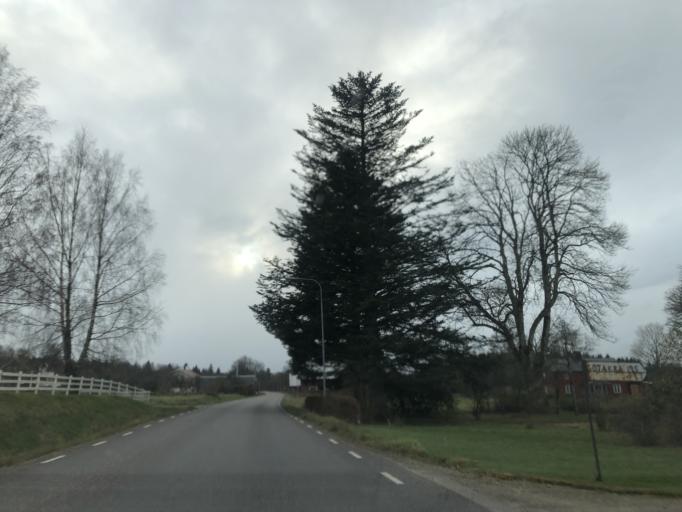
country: SE
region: Vaestra Goetaland
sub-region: Ulricehamns Kommun
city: Ulricehamn
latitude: 57.6841
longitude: 13.4155
